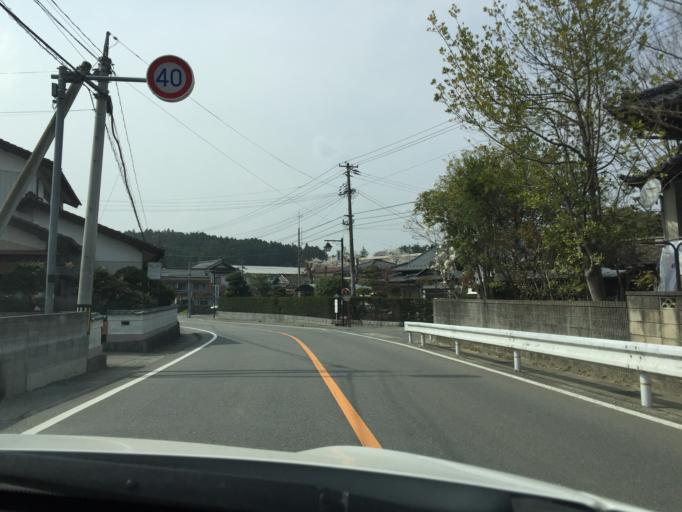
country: JP
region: Fukushima
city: Iwaki
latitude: 37.0079
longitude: 140.7490
